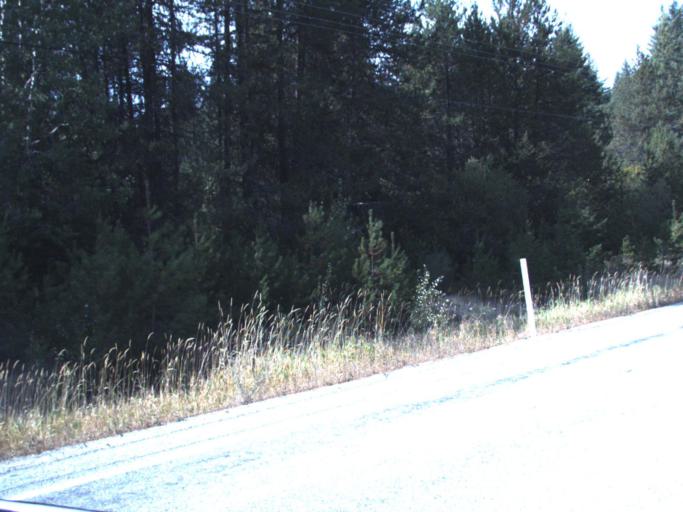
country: US
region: Washington
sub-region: Pend Oreille County
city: Newport
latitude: 48.2558
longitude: -117.2845
